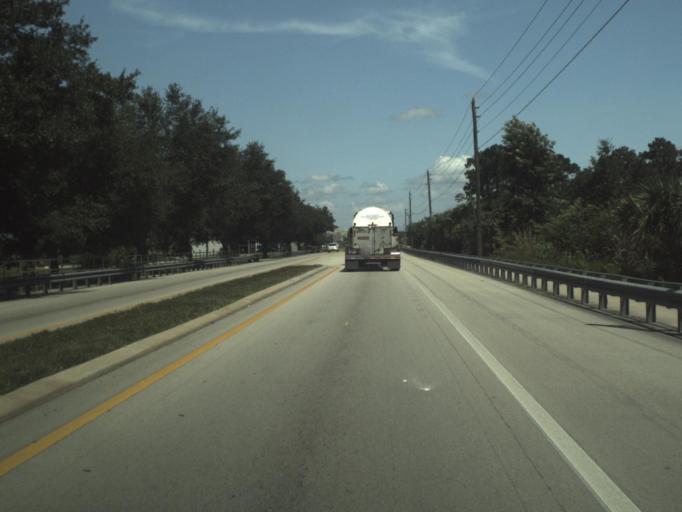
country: US
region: Florida
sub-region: Martin County
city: Indiantown
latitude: 27.0260
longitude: -80.4750
